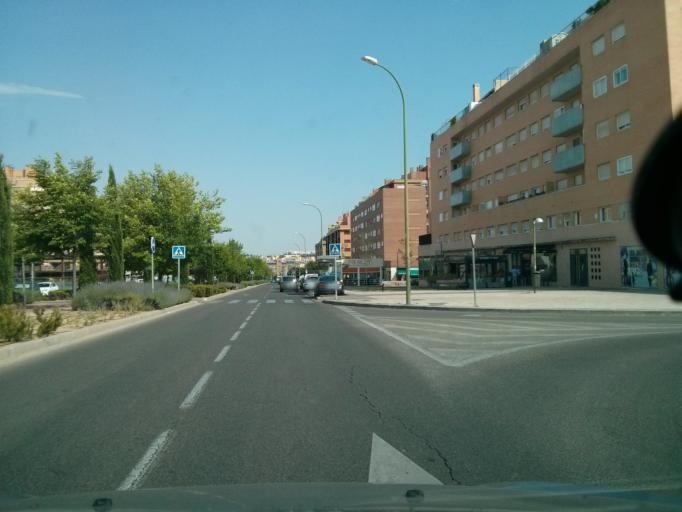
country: ES
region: Madrid
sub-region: Provincia de Madrid
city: Pinar de Chamartin
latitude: 40.4938
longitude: -3.6566
